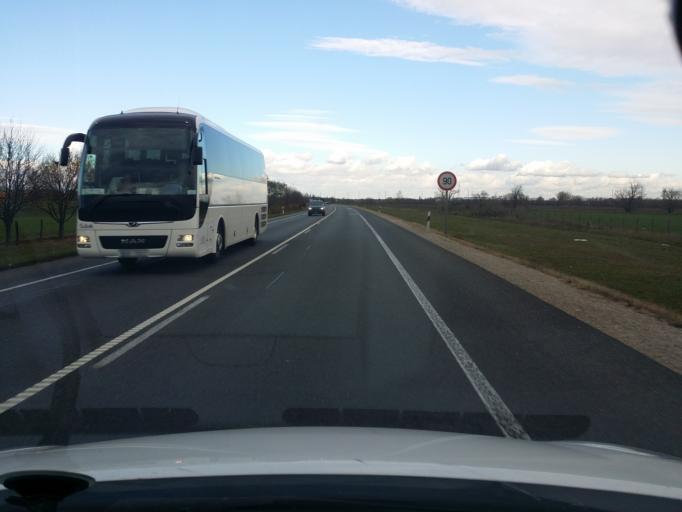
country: HU
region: Gyor-Moson-Sopron
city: Rajka
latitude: 47.9806
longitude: 17.1833
